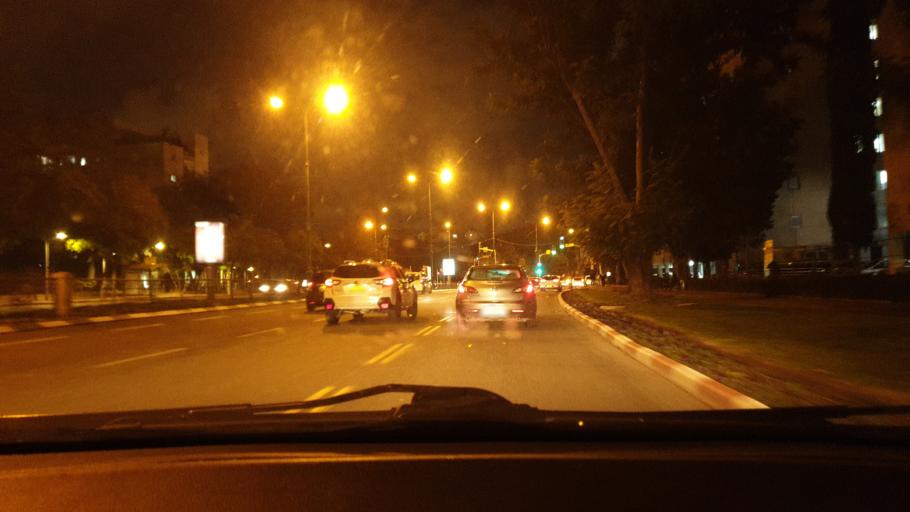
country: IL
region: Central District
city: Rishon LeZiyyon
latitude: 31.9581
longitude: 34.8022
